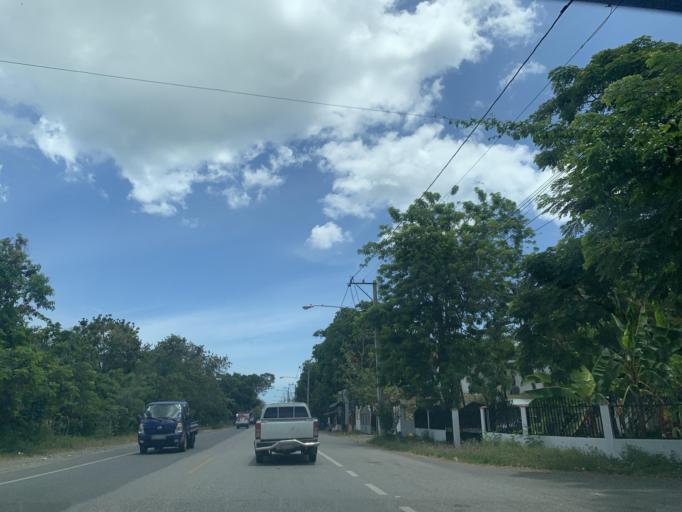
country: DO
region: Puerto Plata
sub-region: Puerto Plata
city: Puerto Plata
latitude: 19.7350
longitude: -70.6042
